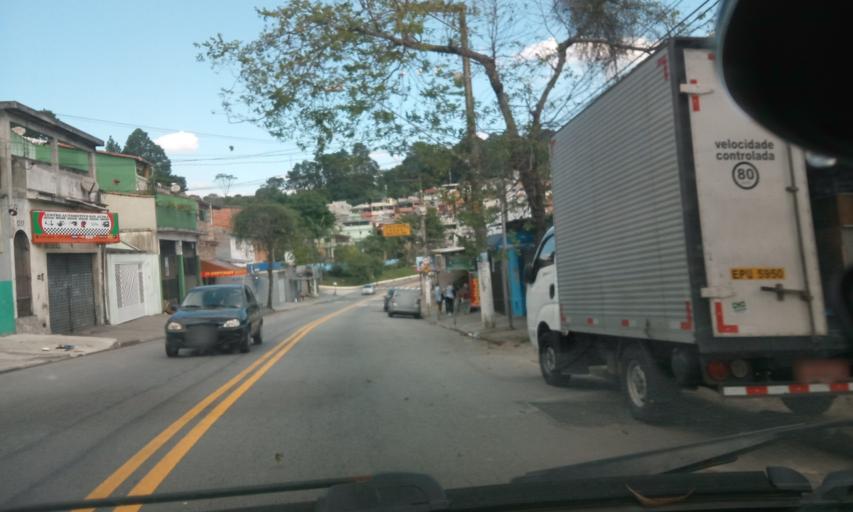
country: BR
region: Sao Paulo
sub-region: Sao Bernardo Do Campo
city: Sao Bernardo do Campo
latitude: -23.7863
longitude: -46.5335
